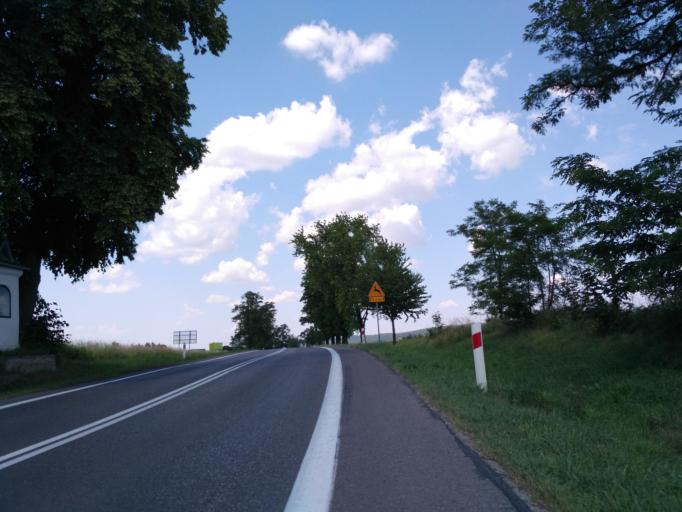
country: PL
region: Subcarpathian Voivodeship
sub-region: Powiat sanocki
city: Strachocina
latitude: 49.6304
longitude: 22.0966
